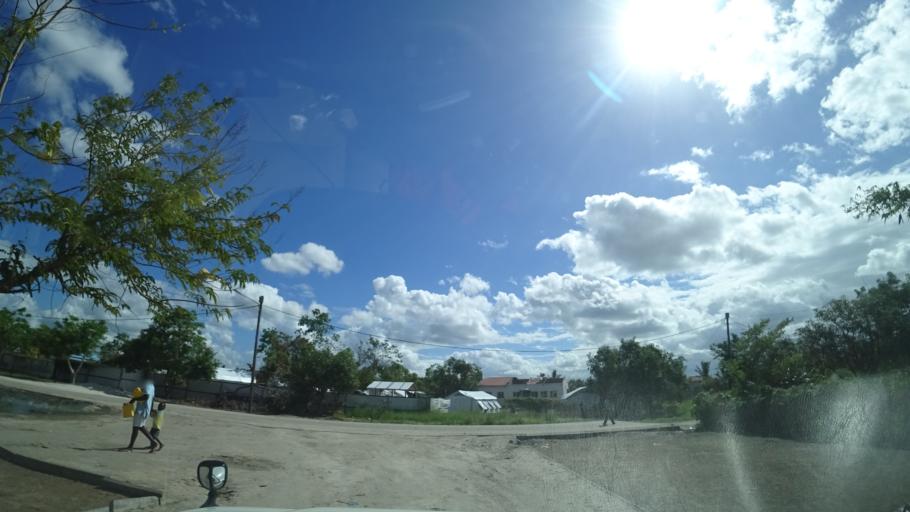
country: MZ
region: Sofala
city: Dondo
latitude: -19.4956
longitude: 34.5986
